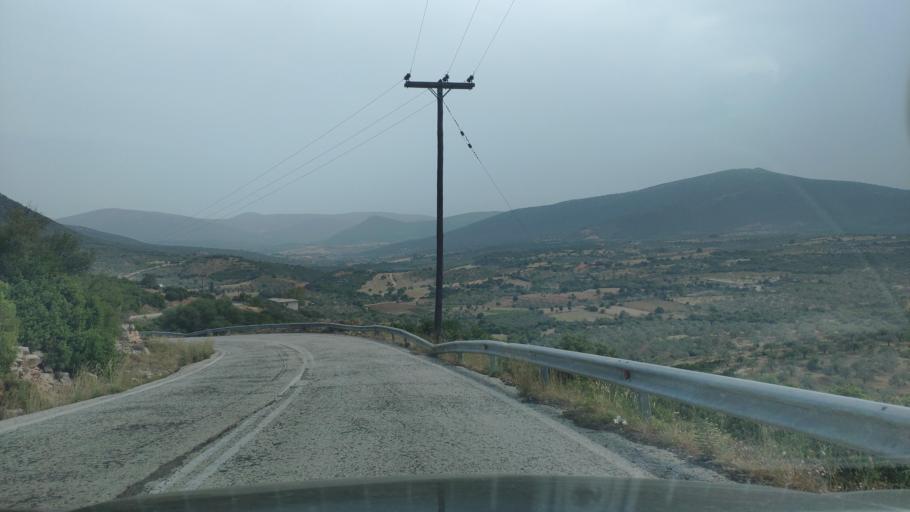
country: GR
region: Peloponnese
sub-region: Nomos Argolidos
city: Palaia Epidavros
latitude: 37.5999
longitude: 23.1569
